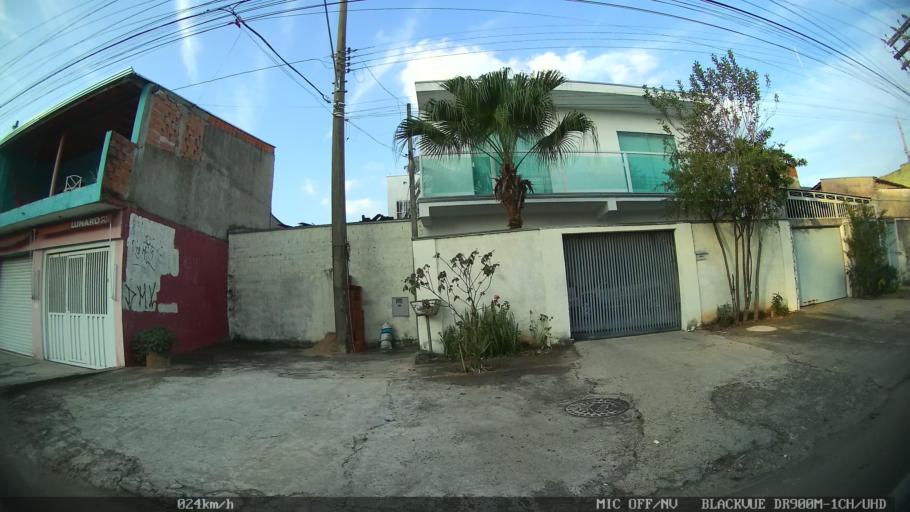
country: BR
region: Sao Paulo
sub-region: Hortolandia
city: Hortolandia
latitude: -22.8812
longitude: -47.1500
